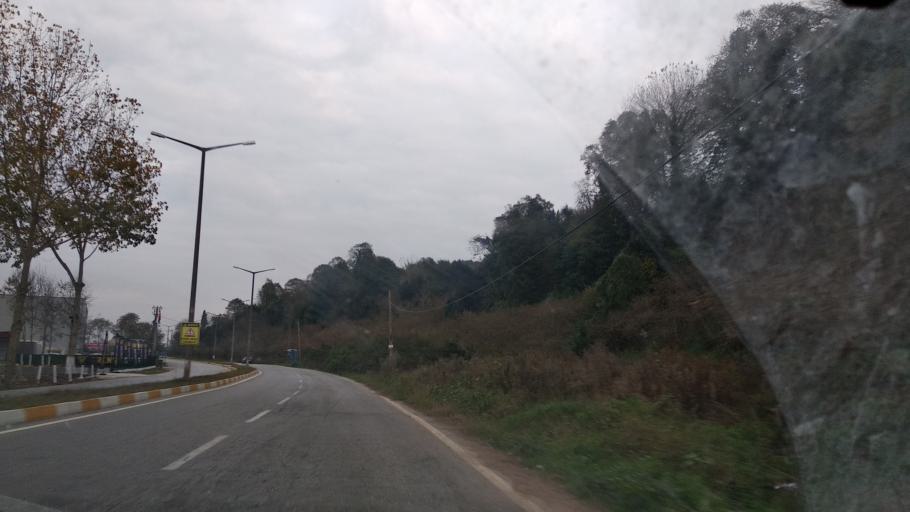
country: TR
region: Sakarya
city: Karasu
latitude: 41.1003
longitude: 30.6642
